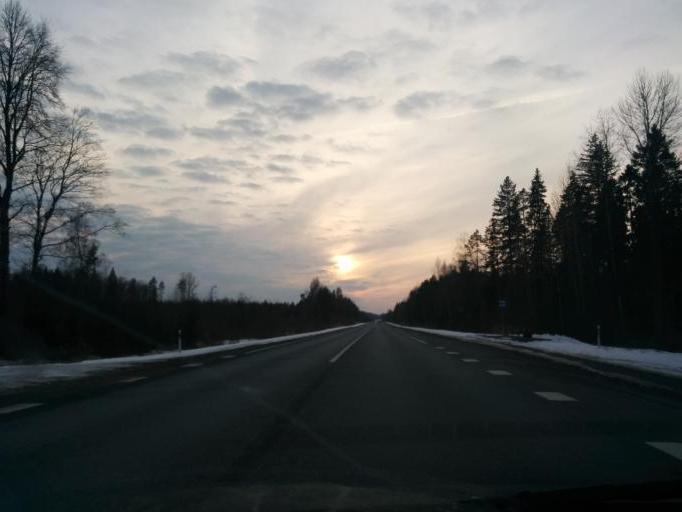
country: LV
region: Raunas
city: Rauna
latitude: 57.3036
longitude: 25.6070
